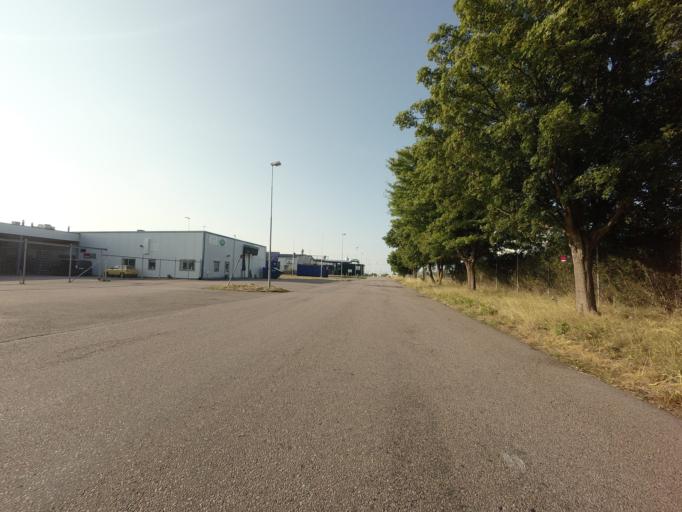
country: SE
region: Skane
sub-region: Landskrona
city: Landskrona
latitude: 55.8693
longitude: 12.8747
